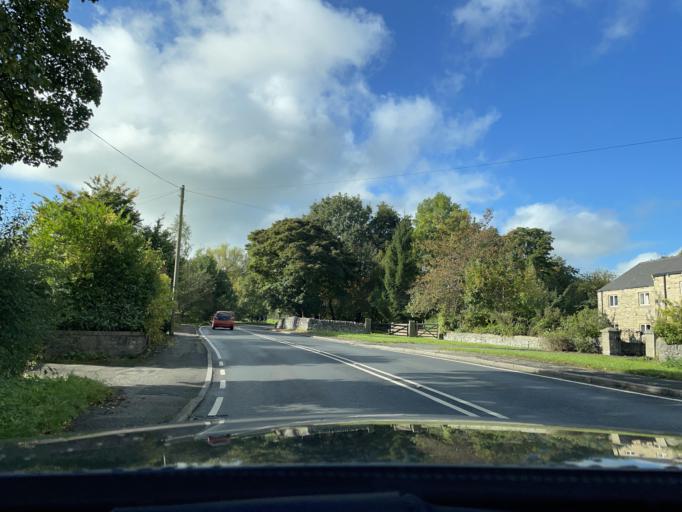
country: GB
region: England
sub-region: Derbyshire
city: Hope Valley
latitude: 53.3477
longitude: -1.7577
